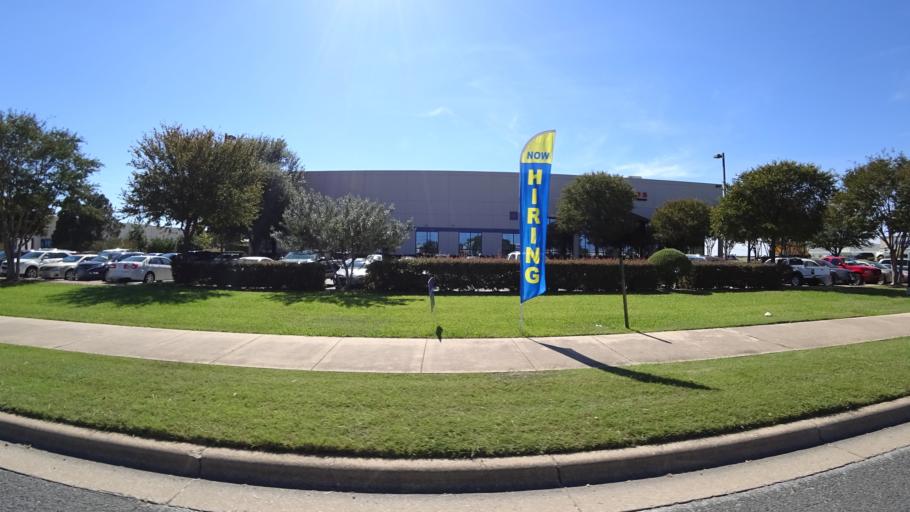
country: US
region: Texas
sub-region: Travis County
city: Austin
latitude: 30.2047
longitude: -97.7150
